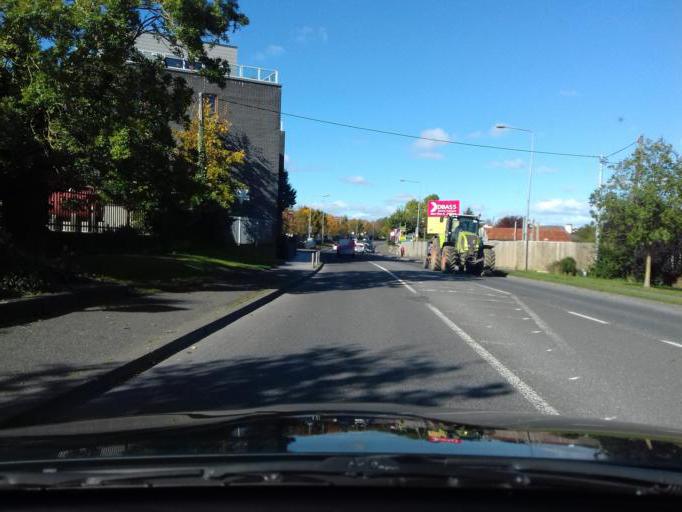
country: IE
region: Leinster
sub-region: An Mhi
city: Ashbourne
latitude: 53.5140
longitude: -6.4023
